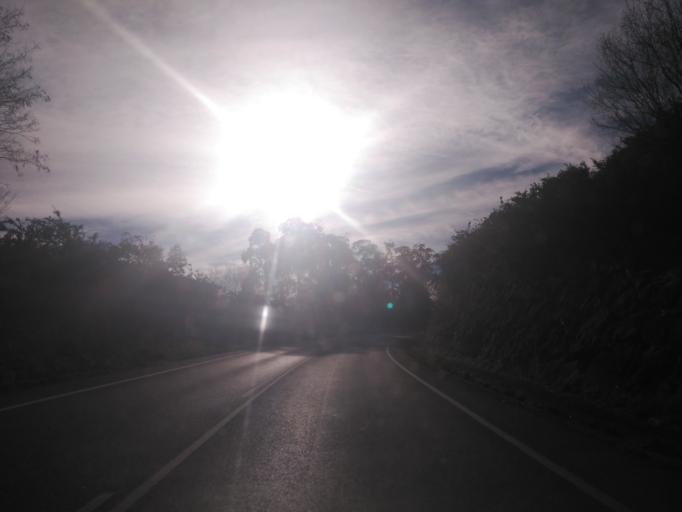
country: ES
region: Cantabria
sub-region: Provincia de Cantabria
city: Comillas
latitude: 43.3695
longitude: -4.2786
